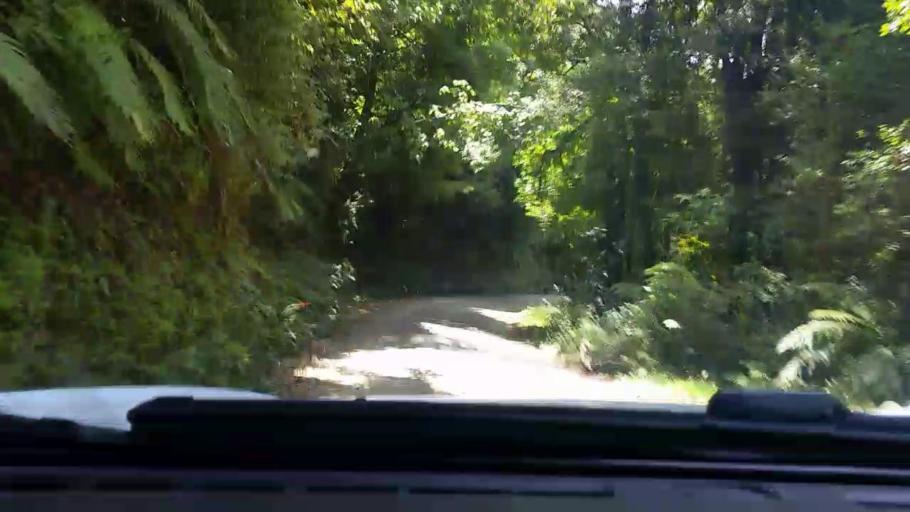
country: NZ
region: Bay of Plenty
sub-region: Kawerau District
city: Kawerau
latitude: -38.0185
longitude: 176.5891
